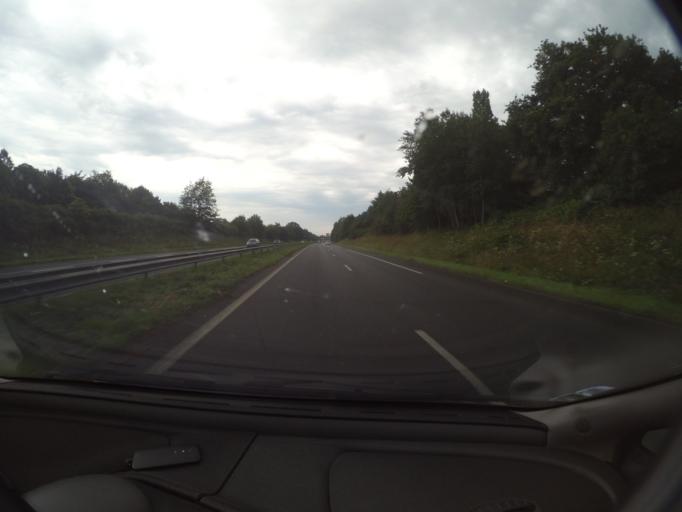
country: FR
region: Pays de la Loire
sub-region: Departement de la Loire-Atlantique
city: Sainte-Luce-sur-Loire
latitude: 47.2761
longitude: -1.4795
